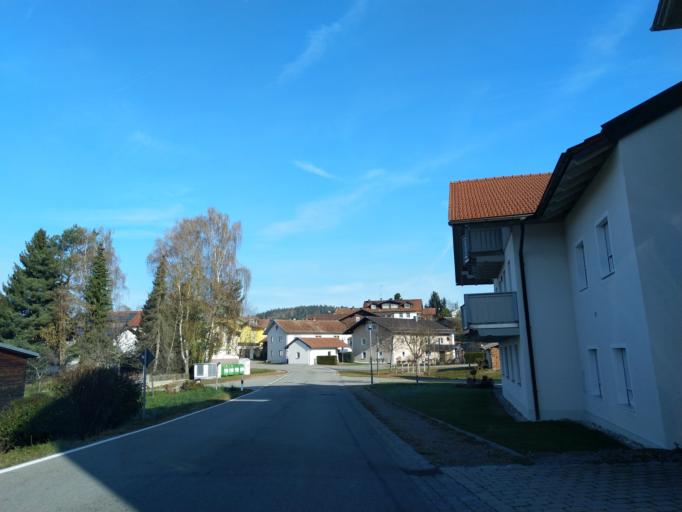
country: DE
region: Bavaria
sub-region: Lower Bavaria
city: Kirchberg
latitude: 48.9040
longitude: 13.1381
